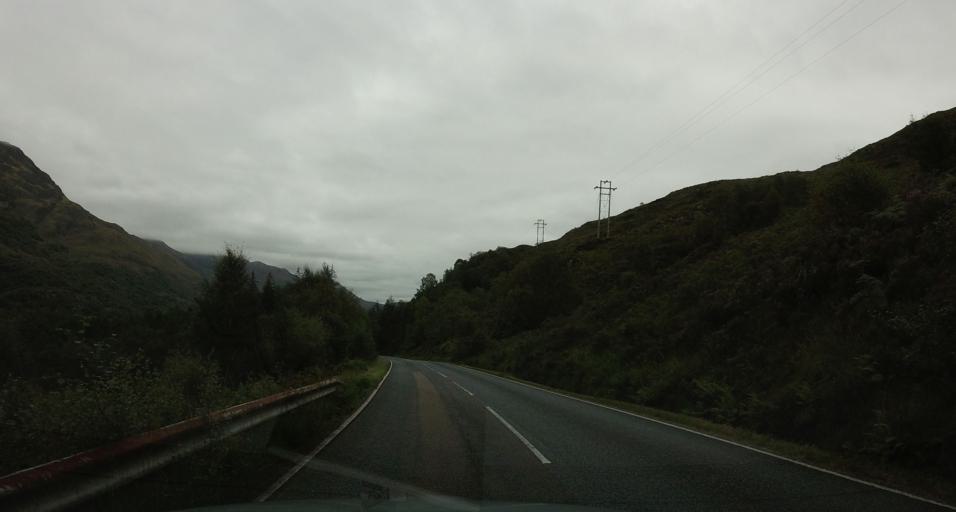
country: GB
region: Scotland
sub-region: Highland
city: Fort William
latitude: 56.6985
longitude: -5.0601
